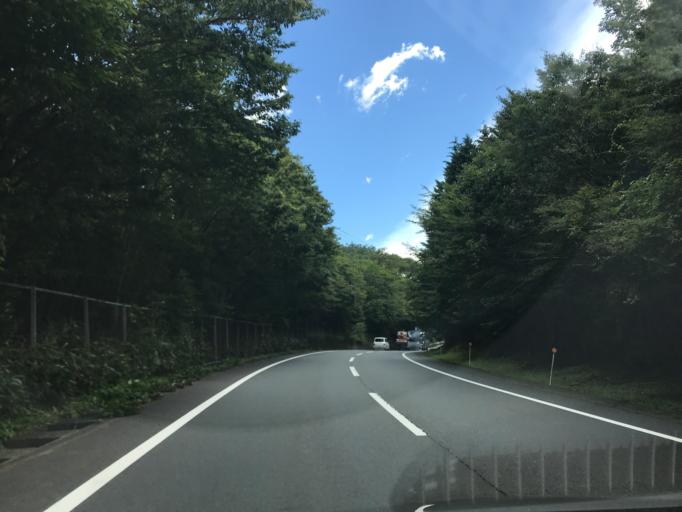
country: JP
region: Shizuoka
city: Gotemba
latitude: 35.2569
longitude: 138.8012
